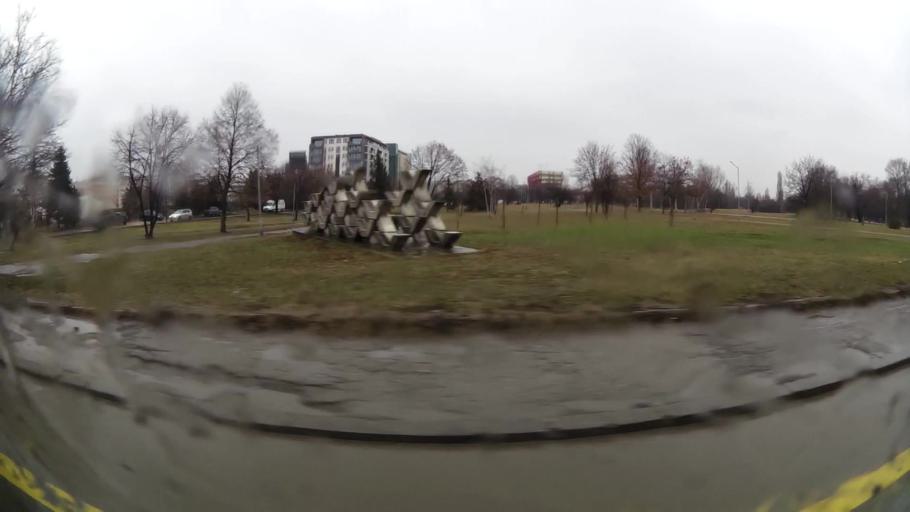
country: BG
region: Sofia-Capital
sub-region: Stolichna Obshtina
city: Sofia
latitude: 42.6565
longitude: 23.3496
